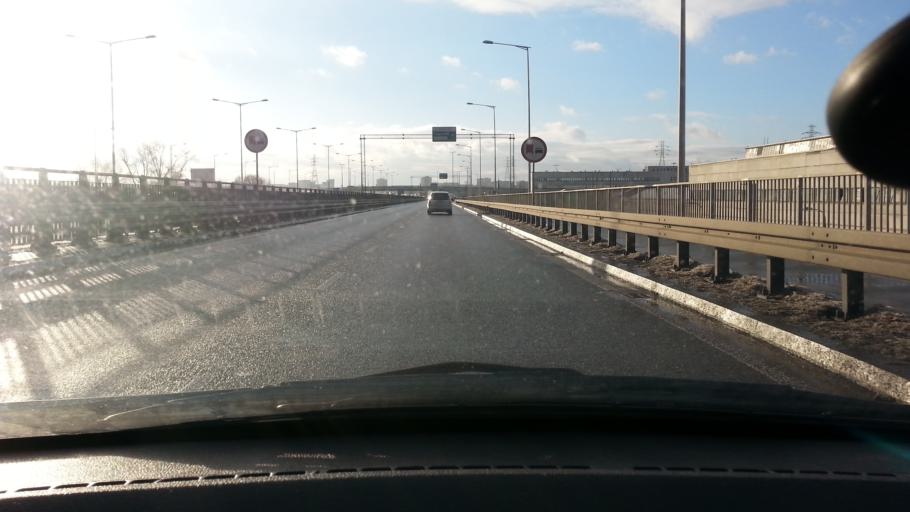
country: PL
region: Masovian Voivodeship
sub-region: Warszawa
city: Zoliborz
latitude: 52.2919
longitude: 21.0091
